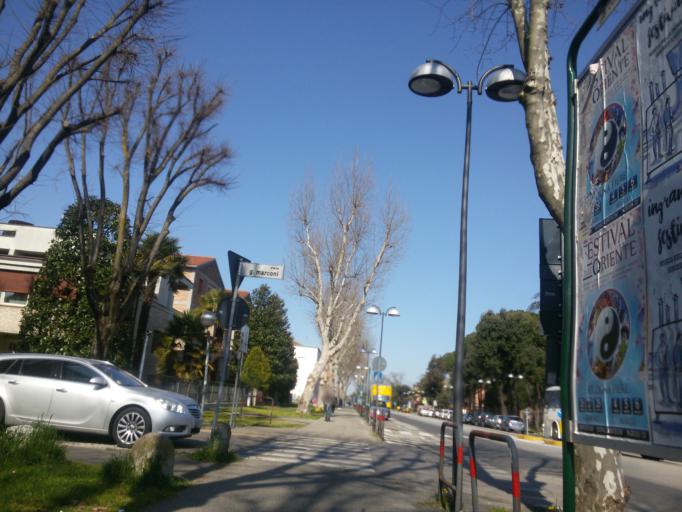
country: IT
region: Emilia-Romagna
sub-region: Provincia di Ravenna
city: Lugo
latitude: 44.4158
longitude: 11.9172
